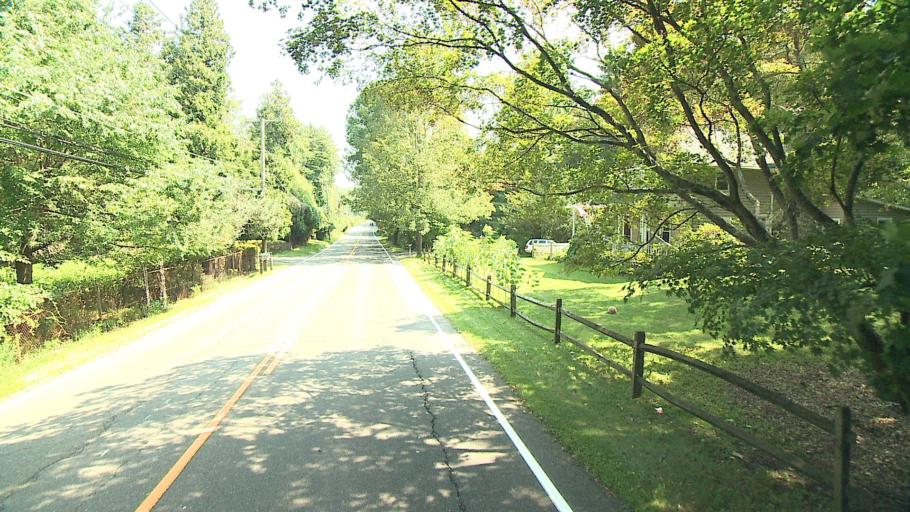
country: US
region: Connecticut
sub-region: Fairfield County
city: Georgetown
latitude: 41.2698
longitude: -73.4504
